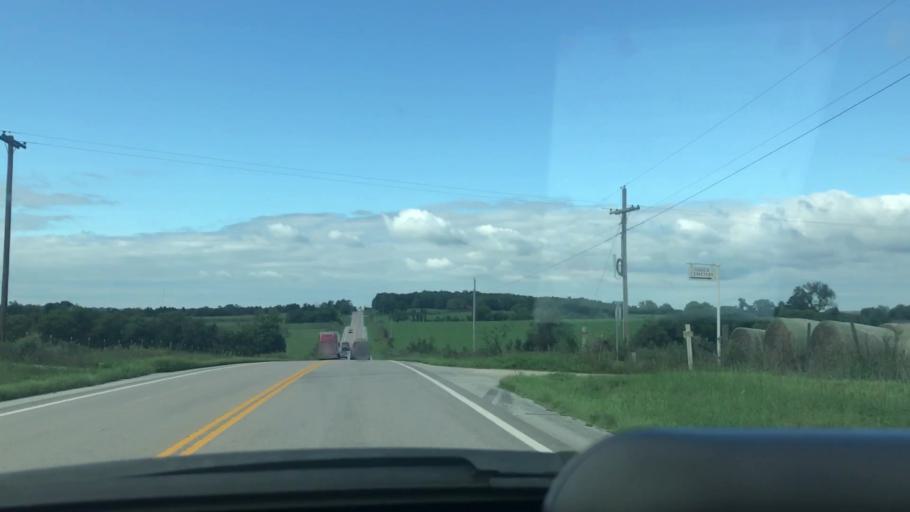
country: US
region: Missouri
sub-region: Hickory County
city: Hermitage
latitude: 37.9552
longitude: -93.2073
